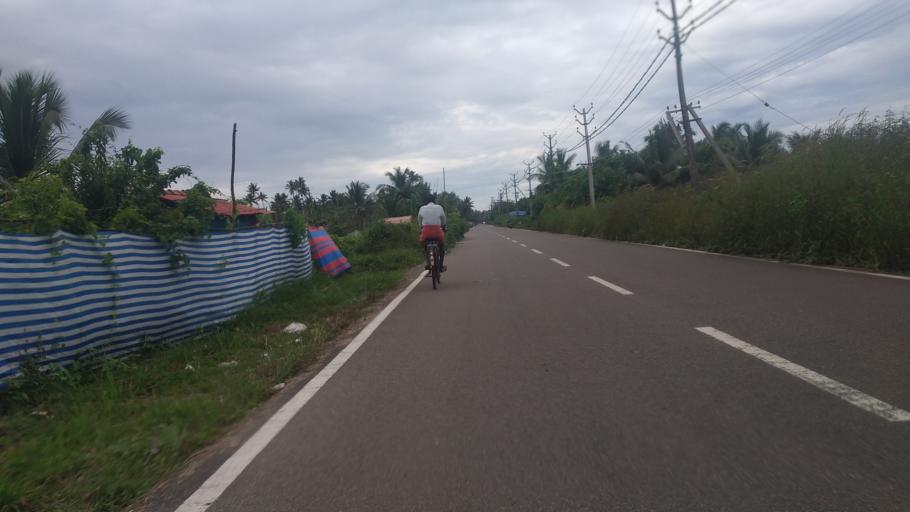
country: IN
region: Kerala
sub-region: Alappuzha
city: Arukutti
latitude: 9.8579
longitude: 76.2697
